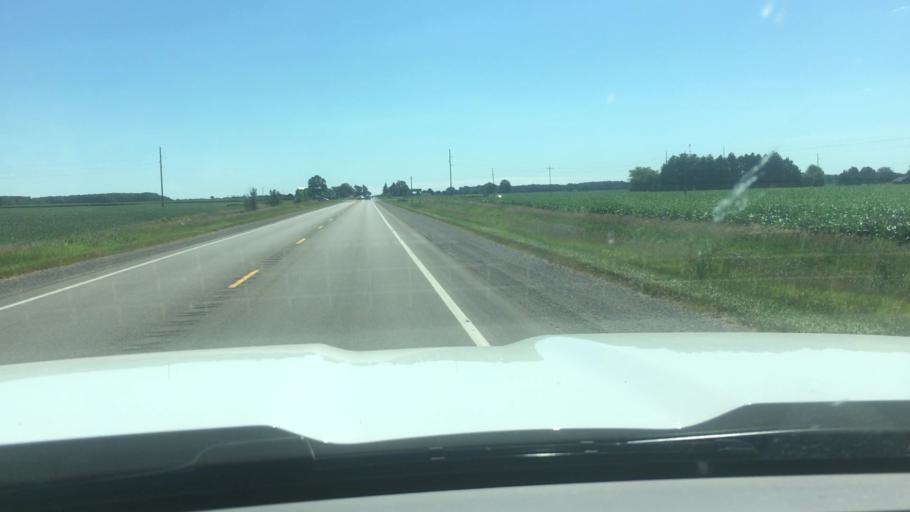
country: US
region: Michigan
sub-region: Montcalm County
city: Carson City
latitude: 43.1764
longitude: -84.7826
